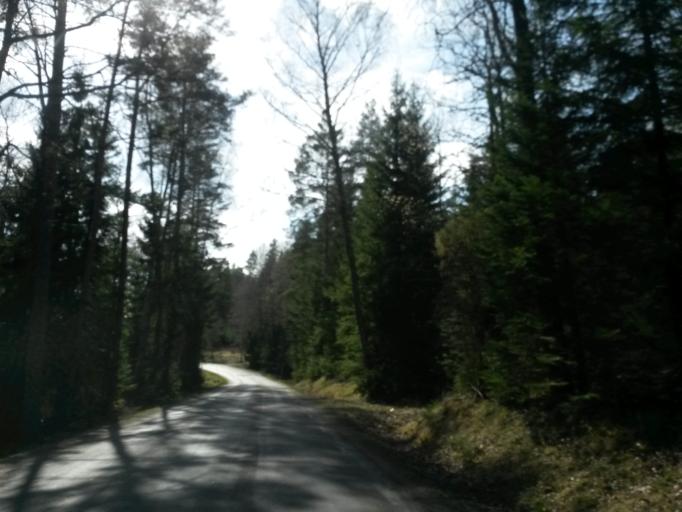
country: SE
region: Vaestra Goetaland
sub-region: Vargarda Kommun
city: Jonstorp
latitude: 57.9499
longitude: 12.7166
